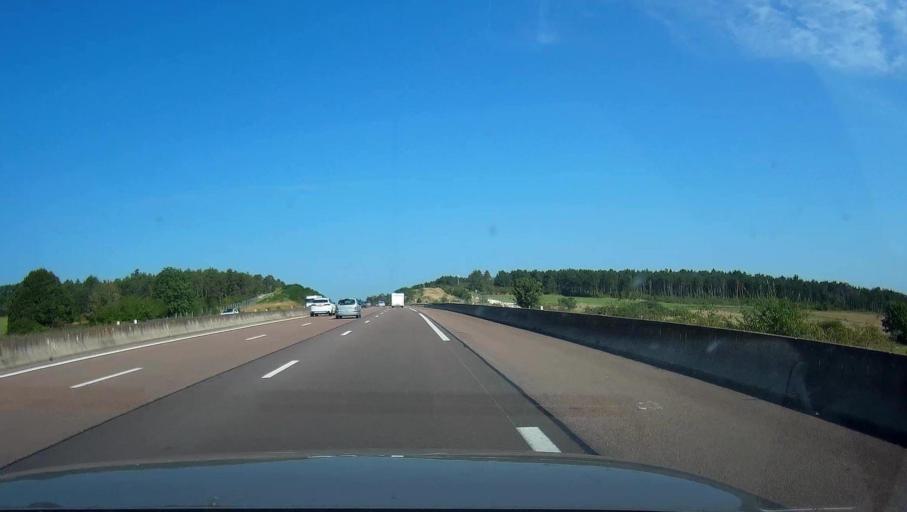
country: FR
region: Bourgogne
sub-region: Departement de la Cote-d'Or
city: Selongey
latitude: 47.5938
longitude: 5.2073
